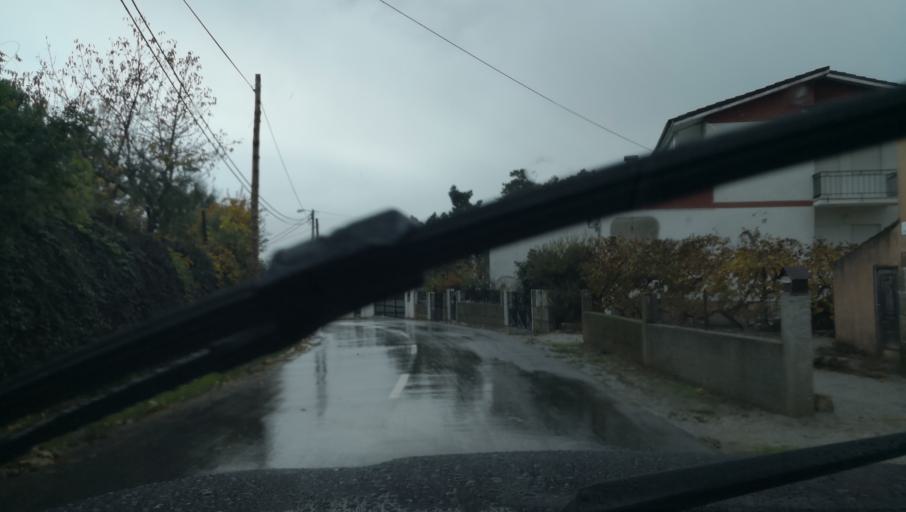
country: PT
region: Vila Real
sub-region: Vila Real
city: Vila Real
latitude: 41.2866
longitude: -7.7099
